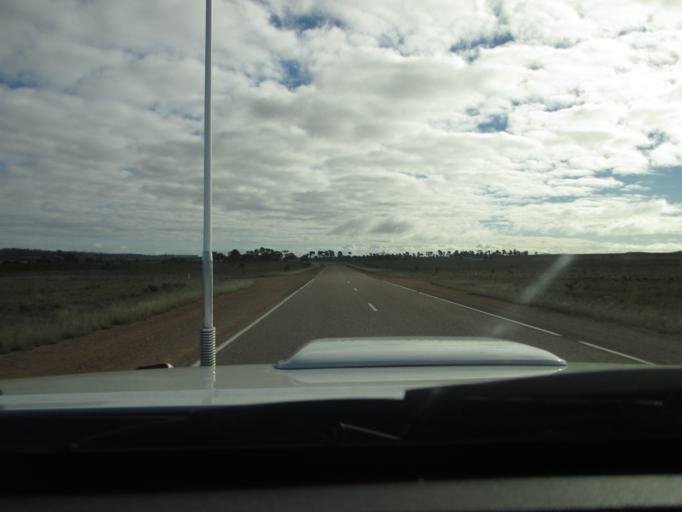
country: AU
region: South Australia
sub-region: Peterborough
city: Peterborough
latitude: -32.5580
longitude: 138.5629
